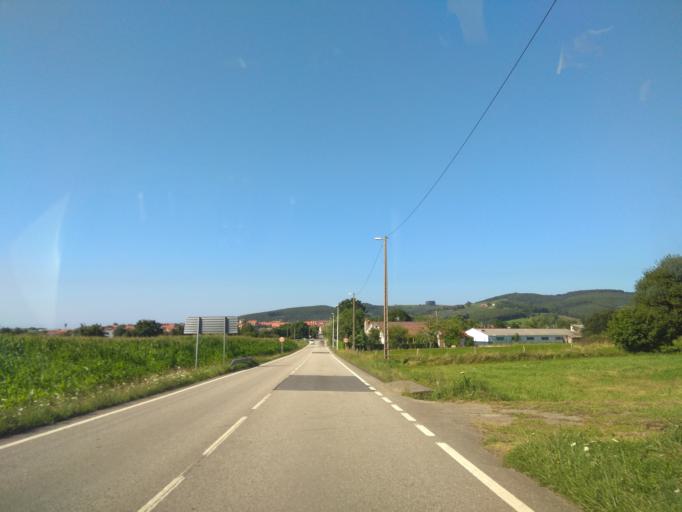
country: ES
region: Cantabria
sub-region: Provincia de Cantabria
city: Bareyo
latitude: 43.4615
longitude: -3.6740
